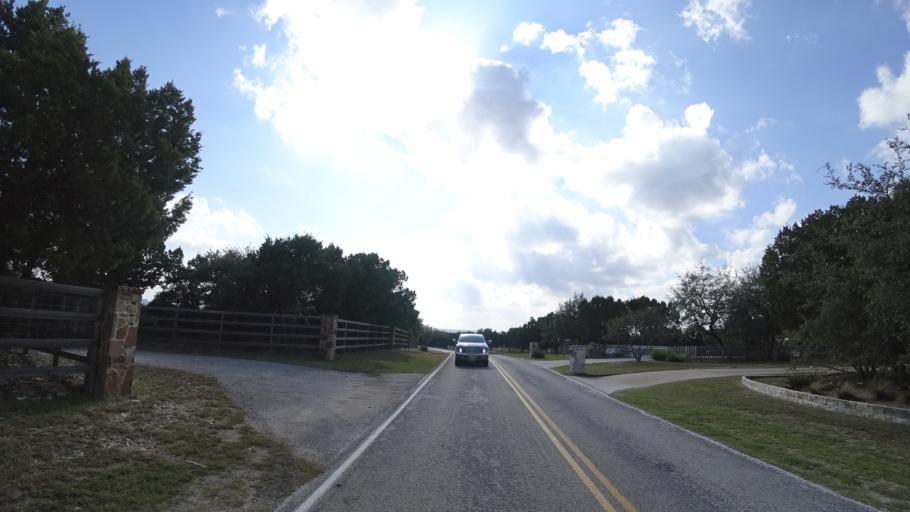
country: US
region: Texas
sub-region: Travis County
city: Lost Creek
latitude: 30.3114
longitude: -97.8652
